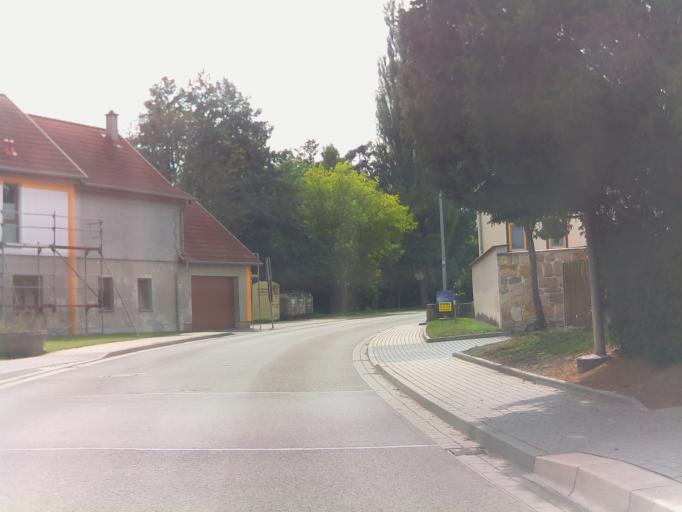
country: DE
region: Thuringia
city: Behringen
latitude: 50.7524
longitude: 11.0411
